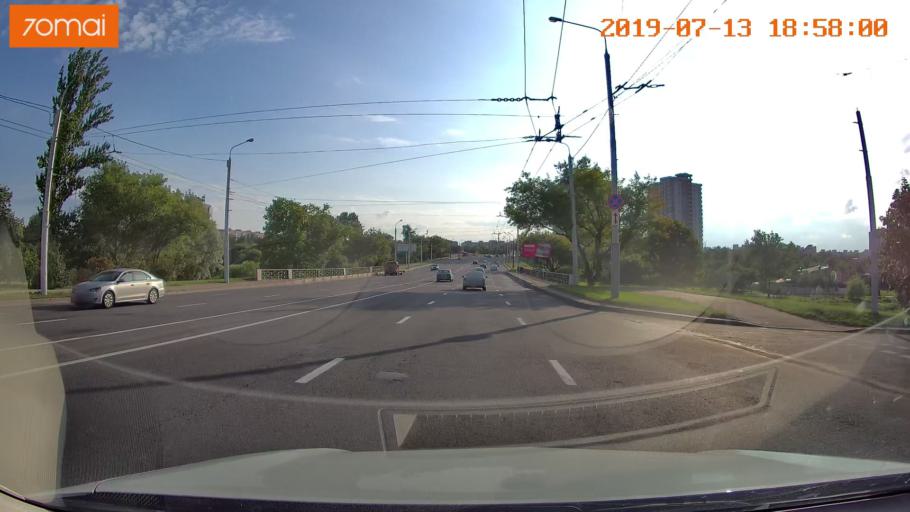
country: BY
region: Minsk
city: Minsk
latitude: 53.8744
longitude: 27.5849
